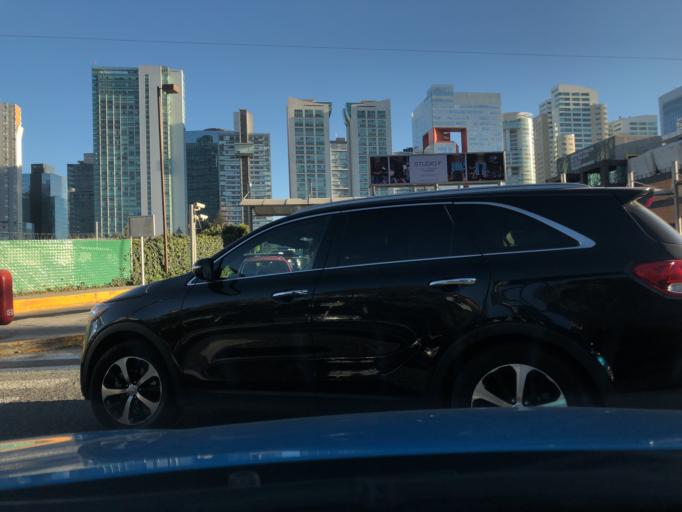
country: MX
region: Mexico City
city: Col. Bosques de las Lomas
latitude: 19.3644
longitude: -99.2706
